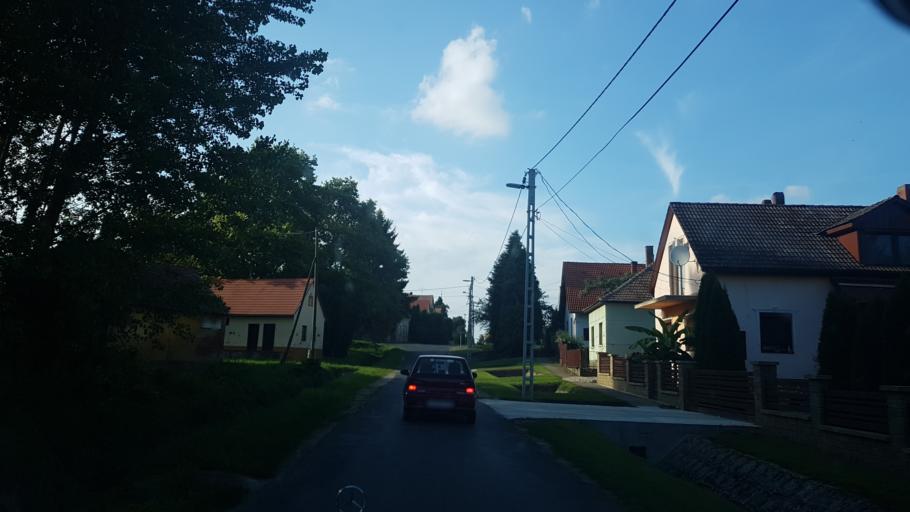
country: HU
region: Somogy
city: Segesd
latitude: 46.3307
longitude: 17.3417
